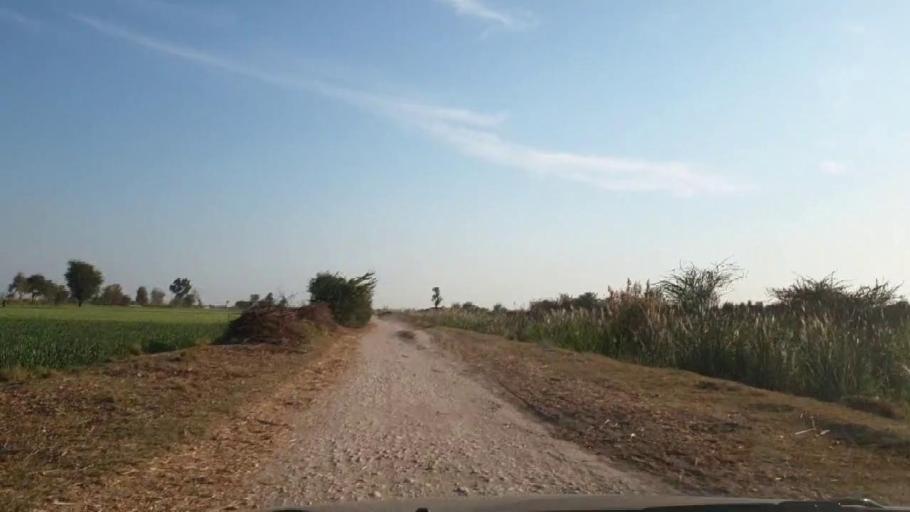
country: PK
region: Sindh
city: Khadro
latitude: 26.2162
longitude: 68.7414
